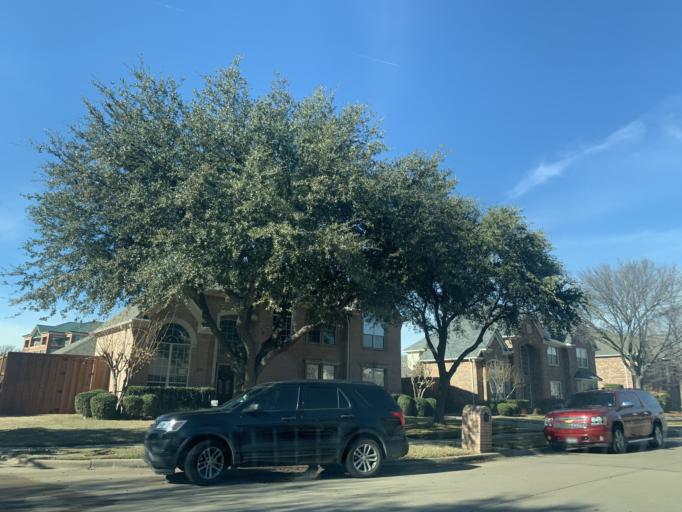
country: US
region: Texas
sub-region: Denton County
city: The Colony
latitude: 33.0504
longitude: -96.8258
